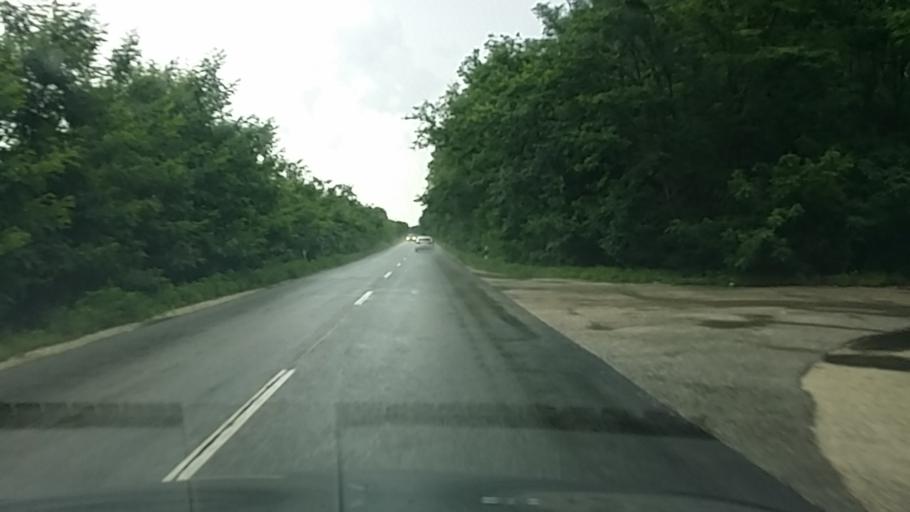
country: HU
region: Pest
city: Ullo
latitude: 47.3355
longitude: 19.3187
